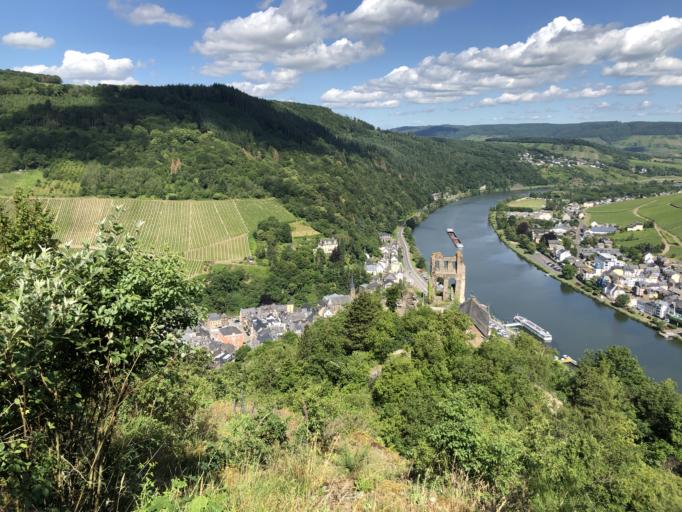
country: DE
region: Rheinland-Pfalz
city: Traben-Trarbach
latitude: 49.9461
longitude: 7.1170
